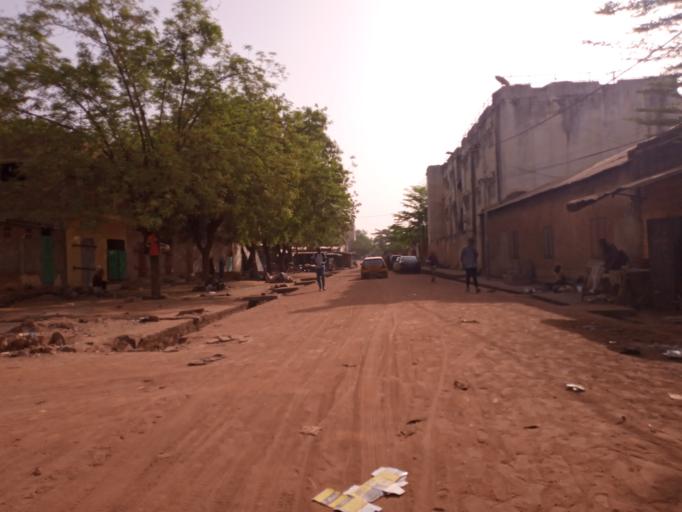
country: ML
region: Bamako
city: Bamako
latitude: 12.6566
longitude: -7.9887
